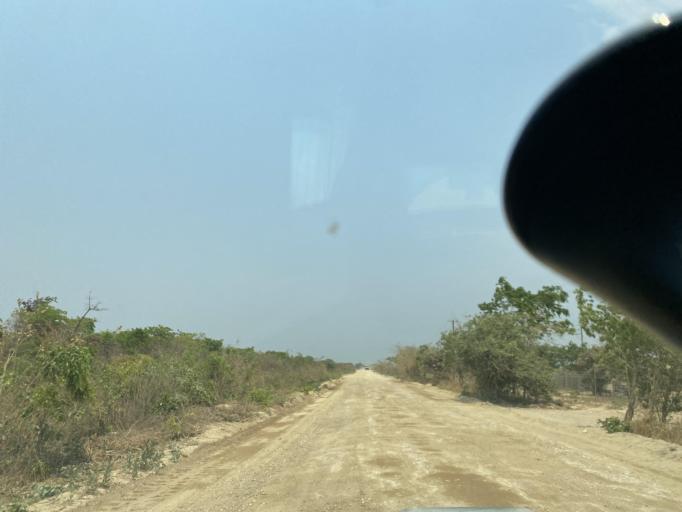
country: ZM
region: Lusaka
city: Lusaka
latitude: -15.5254
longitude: 28.3420
